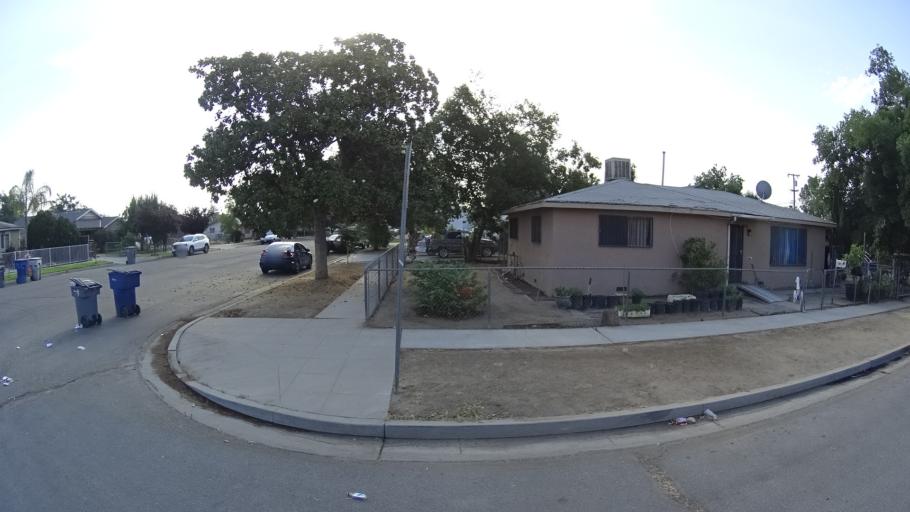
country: US
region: California
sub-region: Fresno County
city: Fresno
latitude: 36.7327
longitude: -119.8115
